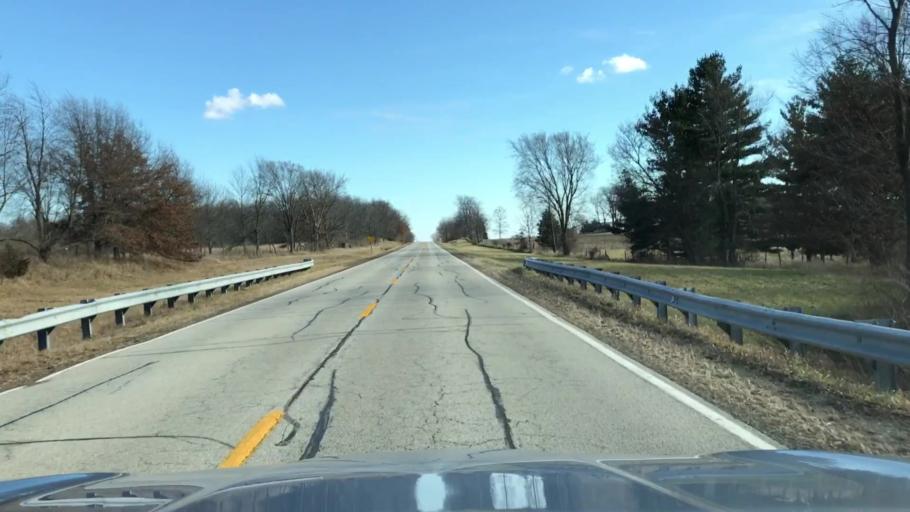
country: US
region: Illinois
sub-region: McLean County
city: Gridley
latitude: 40.6553
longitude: -88.8933
